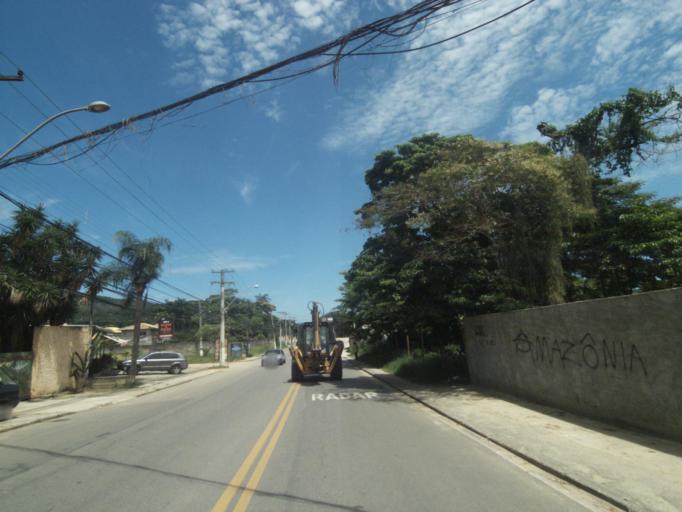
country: BR
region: Rio de Janeiro
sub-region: Niteroi
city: Niteroi
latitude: -22.9407
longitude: -43.0169
